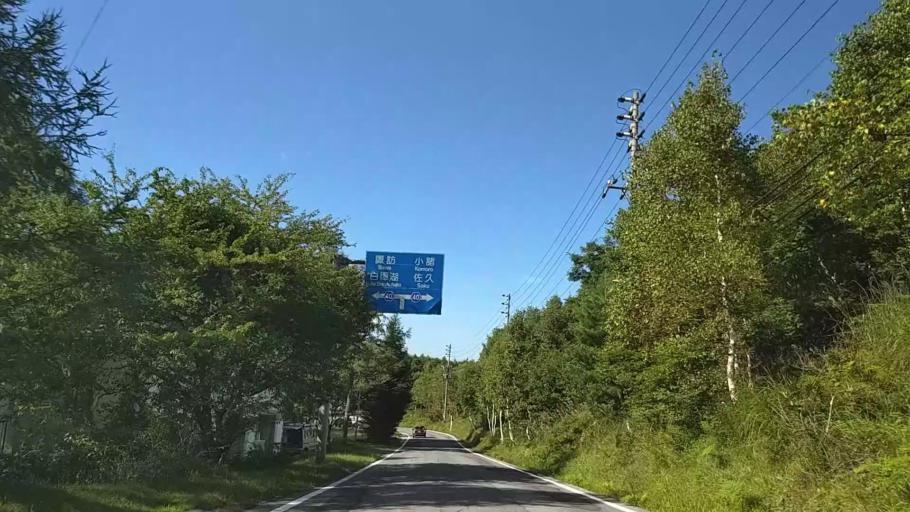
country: JP
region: Nagano
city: Chino
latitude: 36.1102
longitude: 138.2458
